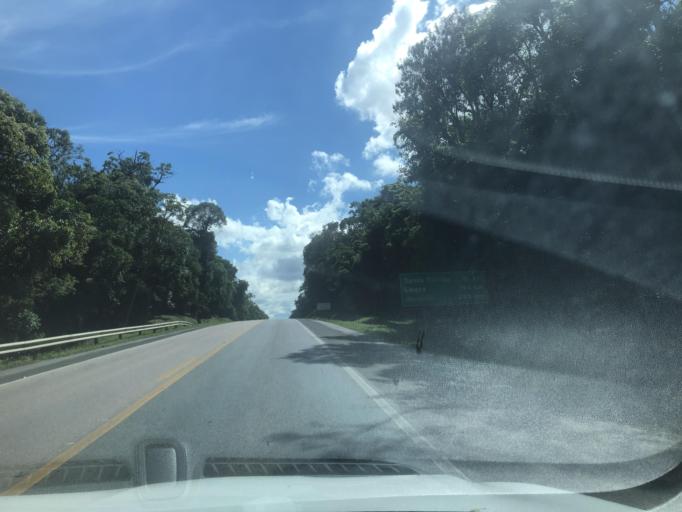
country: BR
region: Santa Catarina
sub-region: Canoinhas
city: Canoinhas
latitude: -26.3841
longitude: -50.2188
